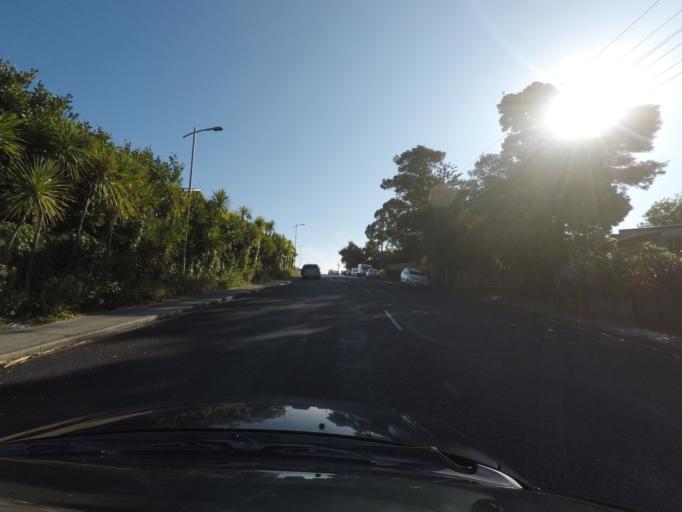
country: NZ
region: Auckland
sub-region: Auckland
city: Rosebank
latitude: -36.8727
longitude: 174.6007
